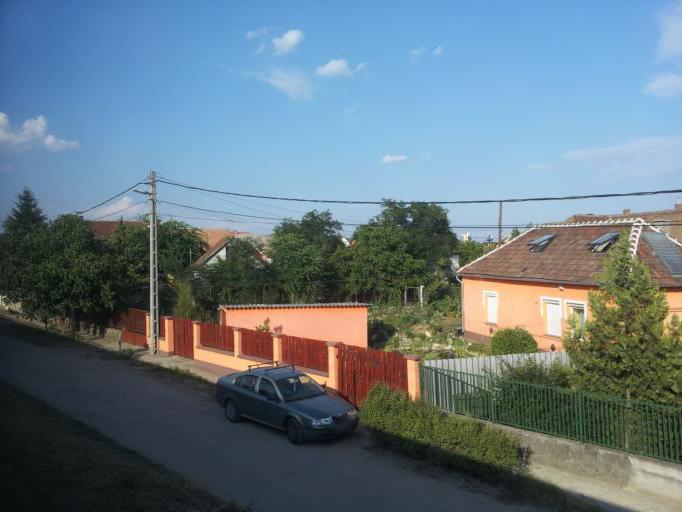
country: HU
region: Pest
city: Dunaharaszti
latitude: 47.3586
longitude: 19.1011
